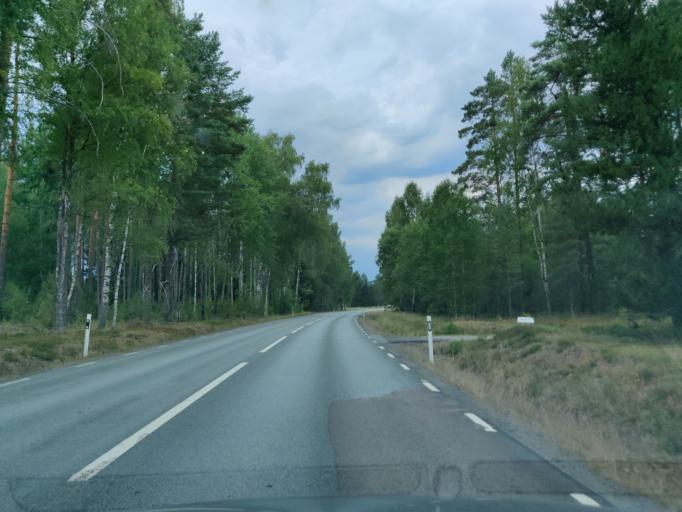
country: SE
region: Vaermland
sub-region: Munkfors Kommun
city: Munkfors
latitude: 59.9616
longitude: 13.5631
